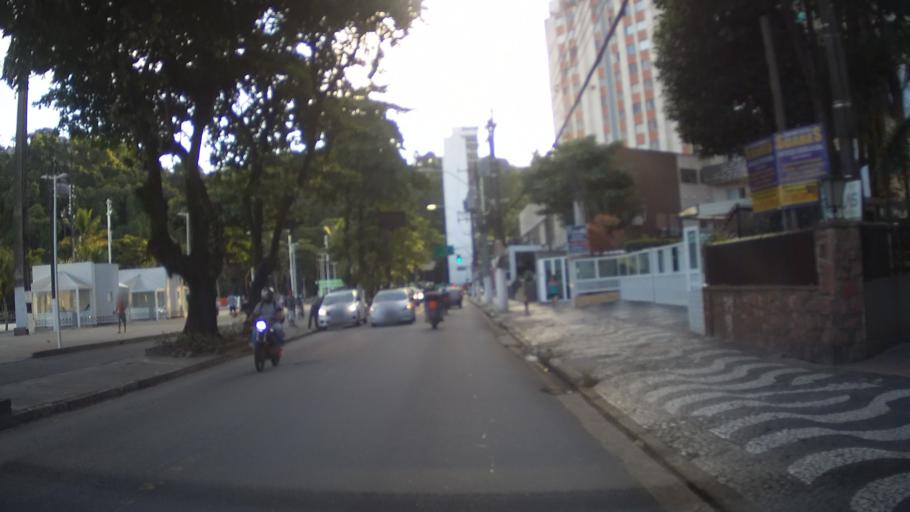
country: BR
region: Sao Paulo
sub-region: Sao Vicente
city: Sao Vicente
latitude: -23.9701
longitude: -46.3840
